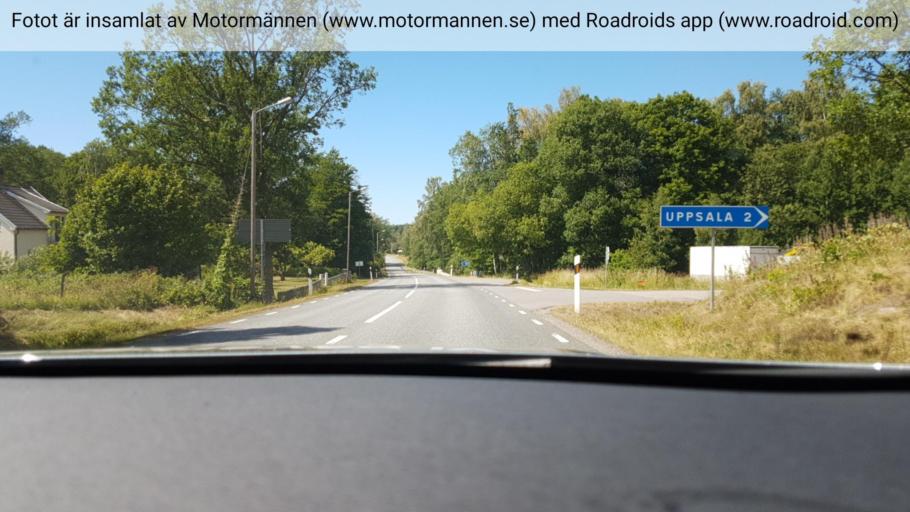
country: SE
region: Joenkoeping
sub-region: Jonkopings Kommun
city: Asa
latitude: 57.9969
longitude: 14.7453
